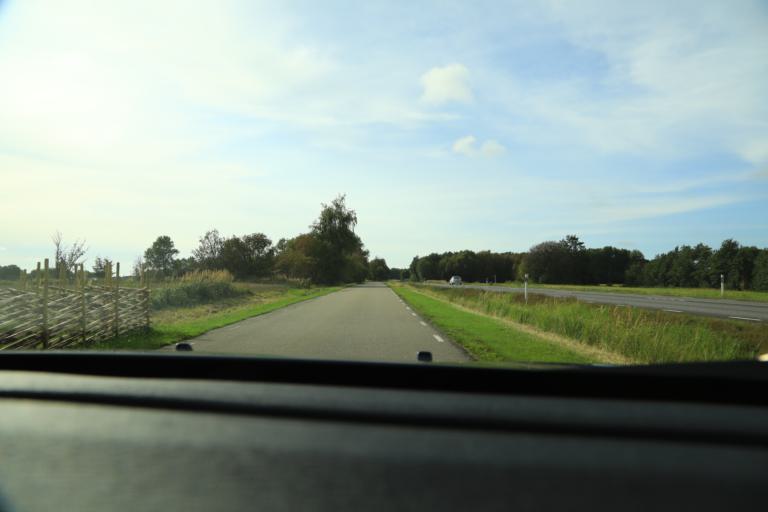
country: SE
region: Halland
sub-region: Varbergs Kommun
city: Traslovslage
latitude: 57.0487
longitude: 12.3216
